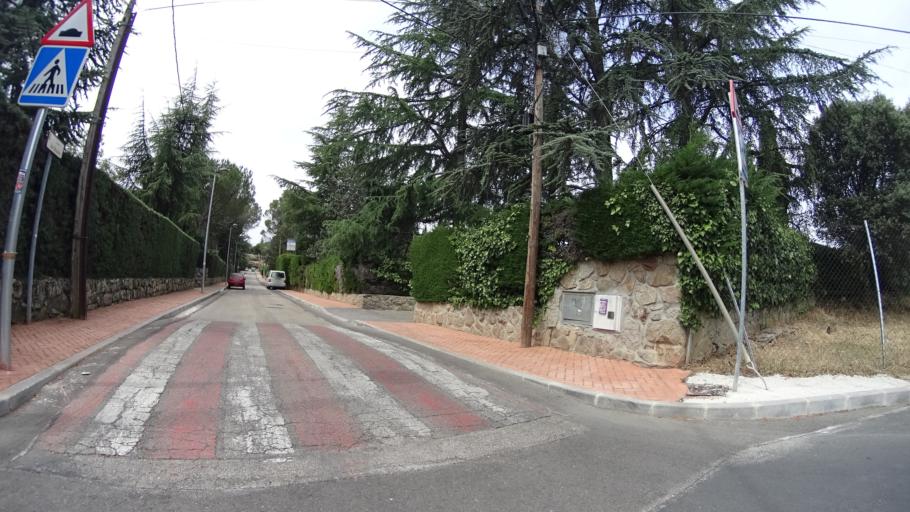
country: ES
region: Madrid
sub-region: Provincia de Madrid
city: Galapagar
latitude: 40.5701
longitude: -4.0018
